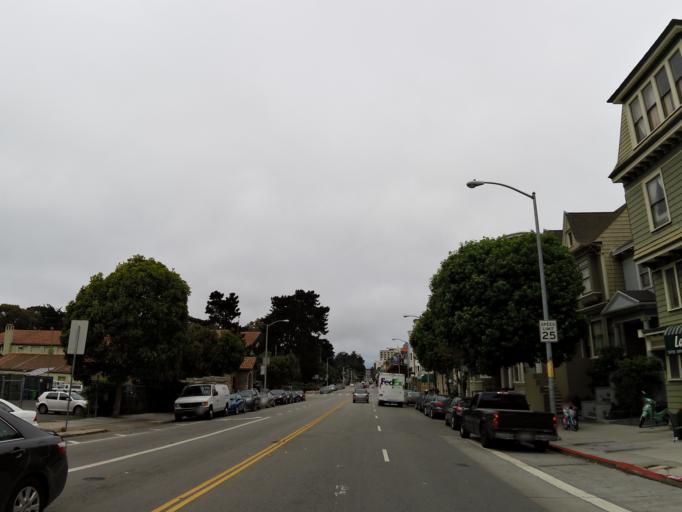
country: US
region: California
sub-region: San Francisco County
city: San Francisco
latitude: 37.7665
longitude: -122.4530
